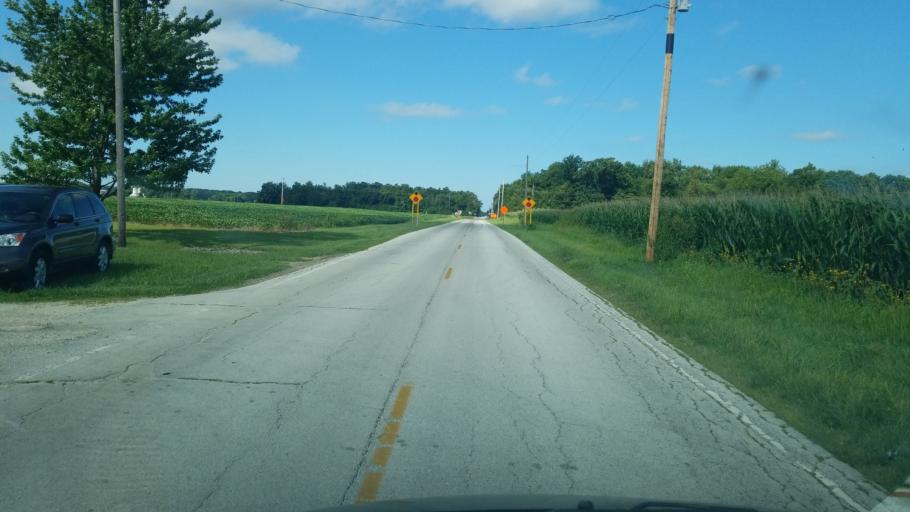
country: US
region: Ohio
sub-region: Seneca County
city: Fostoria
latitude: 41.1080
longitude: -83.4752
